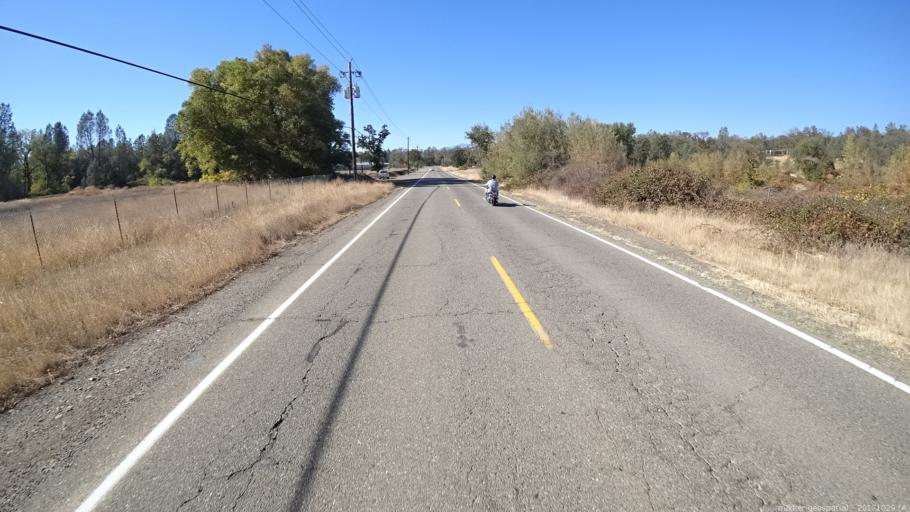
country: US
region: California
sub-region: Shasta County
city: Redding
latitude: 40.5011
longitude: -122.4465
